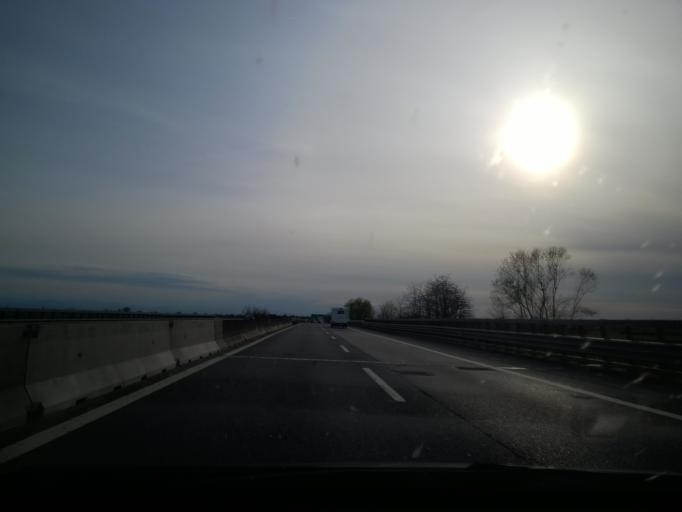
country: IT
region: Emilia-Romagna
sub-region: Provincia di Piacenza
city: Castelvetro Piacentino
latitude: 45.0949
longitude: 10.0117
